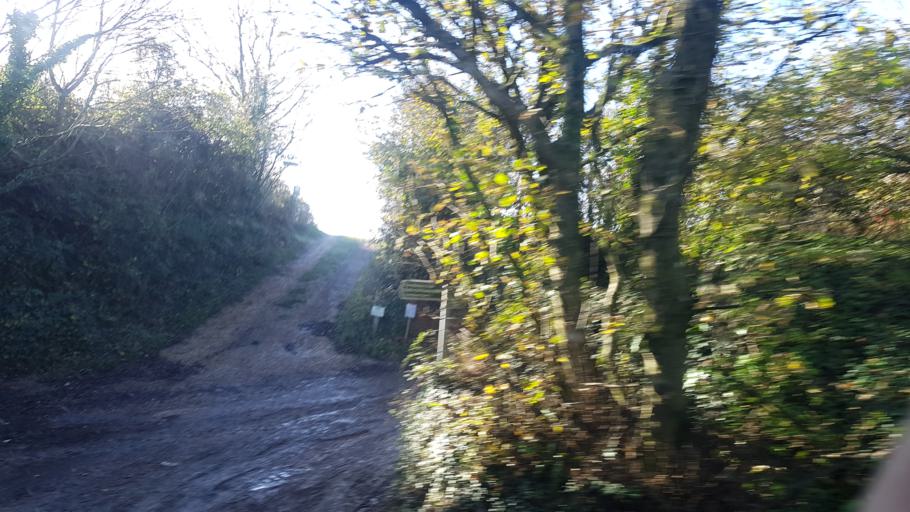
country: GB
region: England
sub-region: Isle of Wight
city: Chale
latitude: 50.6521
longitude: -1.3544
